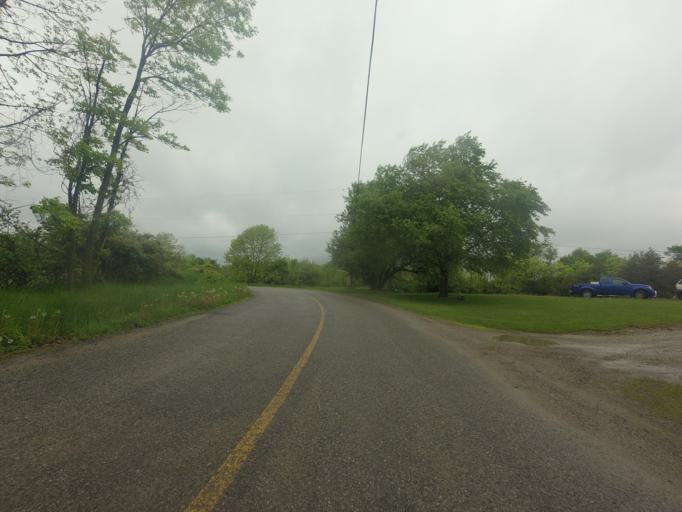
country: CA
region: Ontario
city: Perth
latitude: 44.7088
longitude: -76.1713
